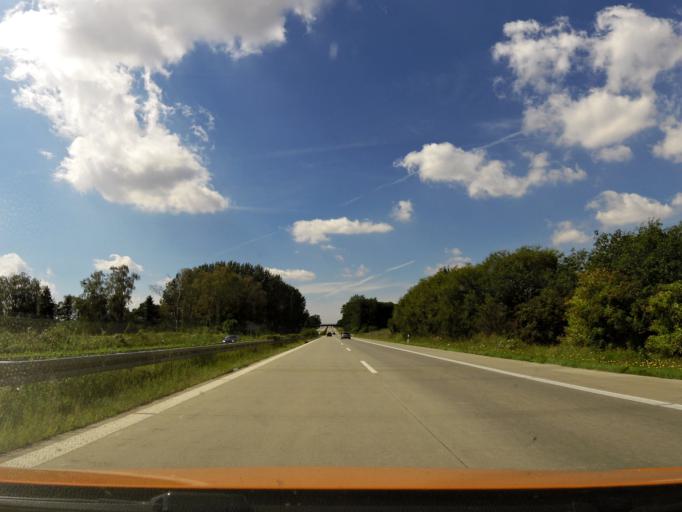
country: DE
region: Mecklenburg-Vorpommern
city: Penkun
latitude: 53.3023
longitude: 14.1892
